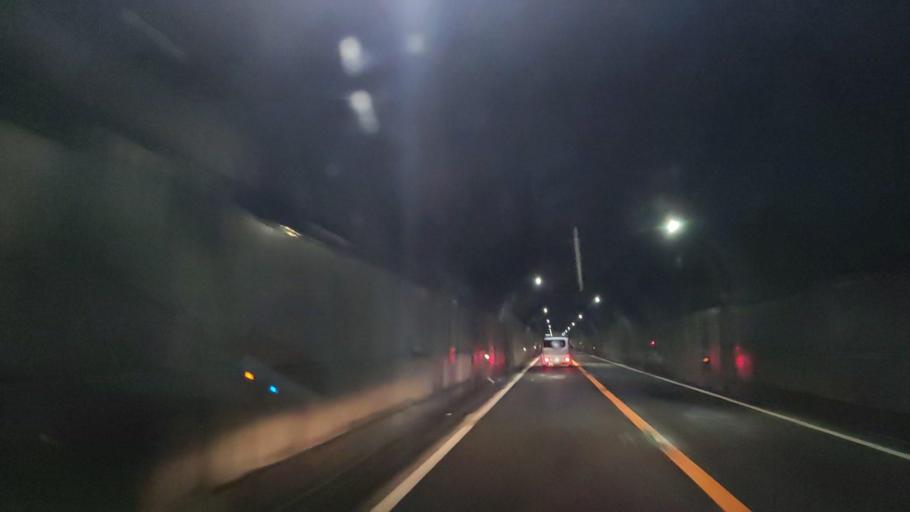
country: JP
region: Okayama
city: Niimi
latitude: 35.1879
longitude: 133.5292
